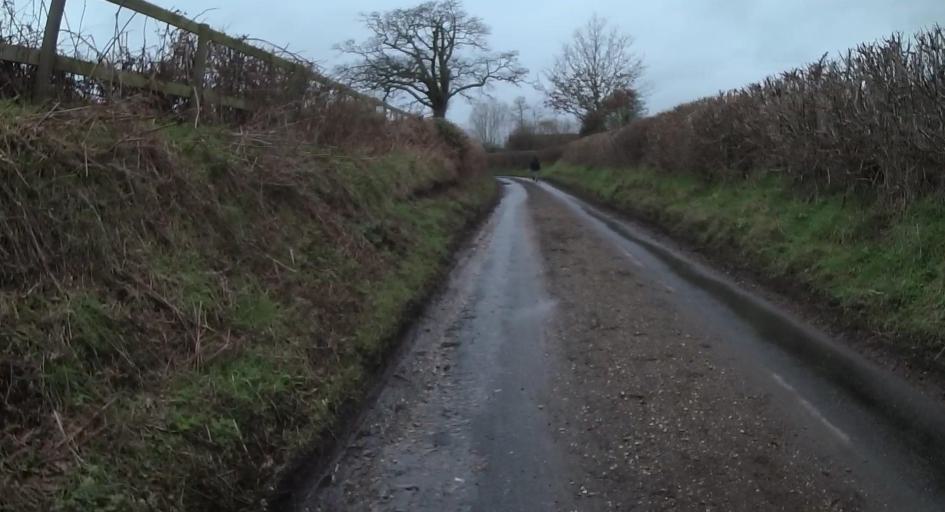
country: GB
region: England
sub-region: West Berkshire
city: Stratfield Mortimer
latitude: 51.3795
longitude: -1.0439
